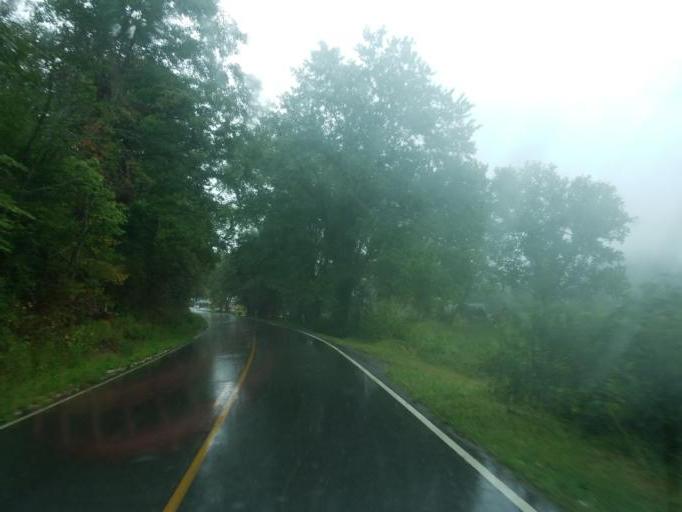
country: US
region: Kentucky
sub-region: Greenup County
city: Greenup
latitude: 38.4993
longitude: -82.9704
